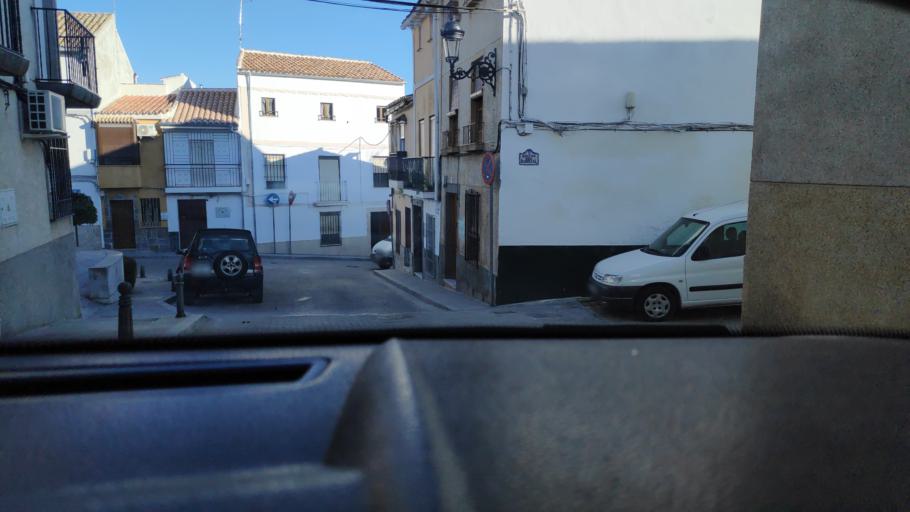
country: ES
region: Andalusia
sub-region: Province of Cordoba
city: Baena
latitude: 37.6141
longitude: -4.3234
